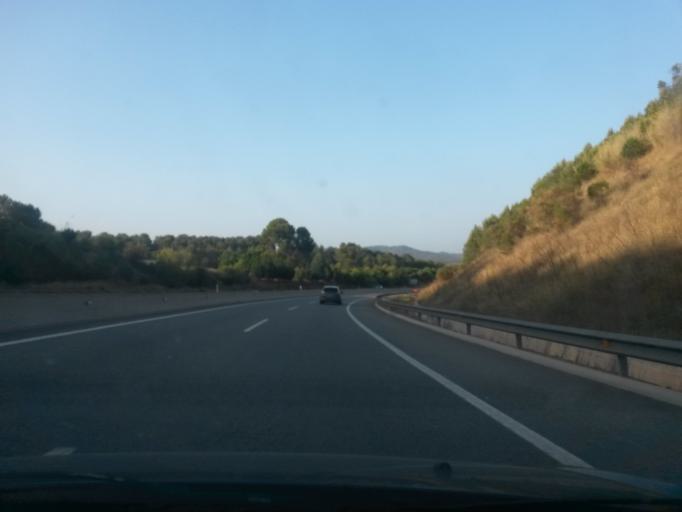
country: ES
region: Catalonia
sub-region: Provincia de Barcelona
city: Palleja
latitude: 41.4118
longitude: 1.9914
